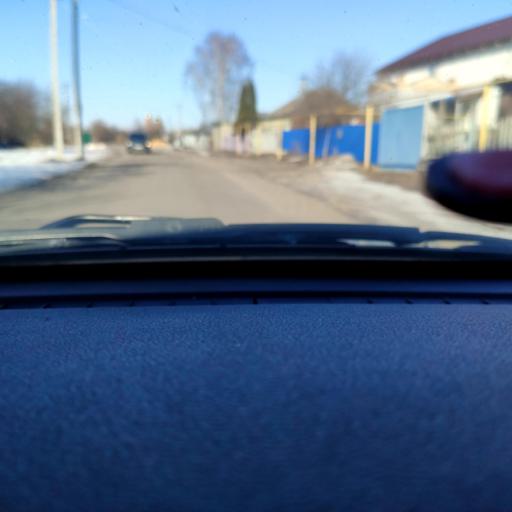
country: RU
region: Voronezj
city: Latnaya
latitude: 51.6970
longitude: 38.9386
